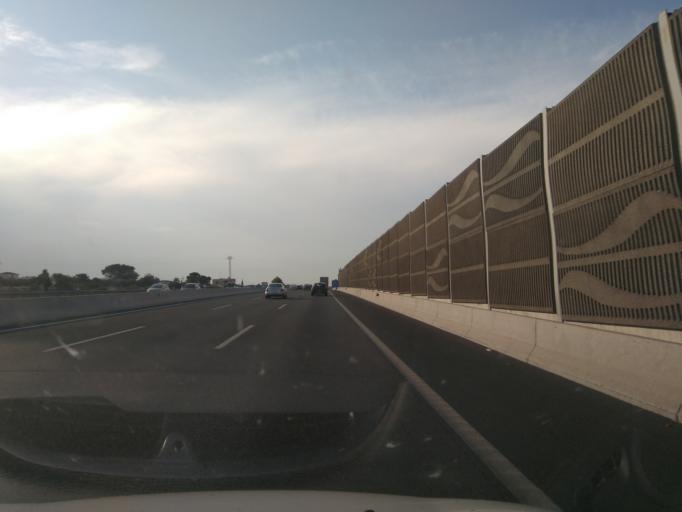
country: ES
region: Valencia
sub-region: Provincia de Valencia
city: Picassent
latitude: 39.3877
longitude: -0.4785
